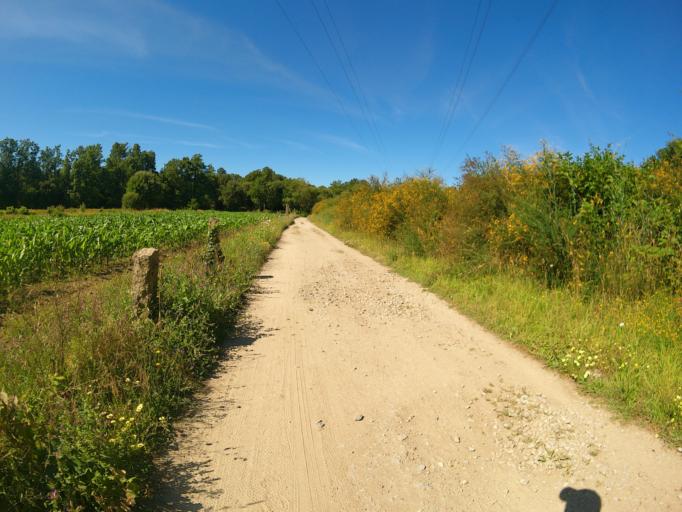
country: PT
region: Viana do Castelo
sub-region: Ponte de Lima
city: Ponte de Lima
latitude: 41.7296
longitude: -8.6646
